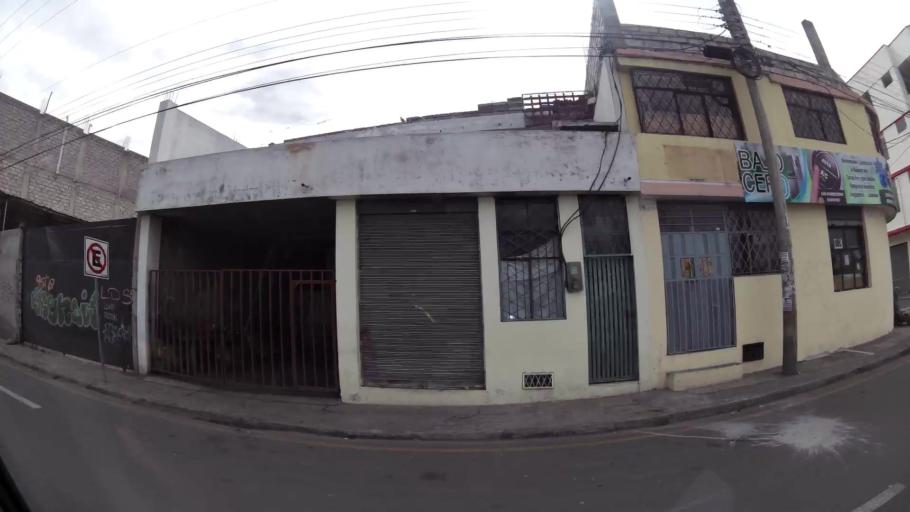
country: EC
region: Cotopaxi
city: Latacunga
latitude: -0.9369
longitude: -78.6202
